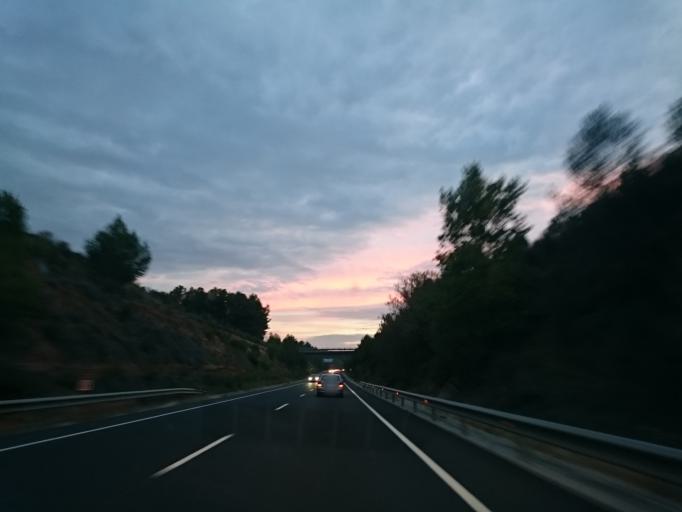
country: ES
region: Catalonia
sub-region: Provincia de Barcelona
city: Sant Pere de Riudebitlles
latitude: 41.4890
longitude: 1.7040
